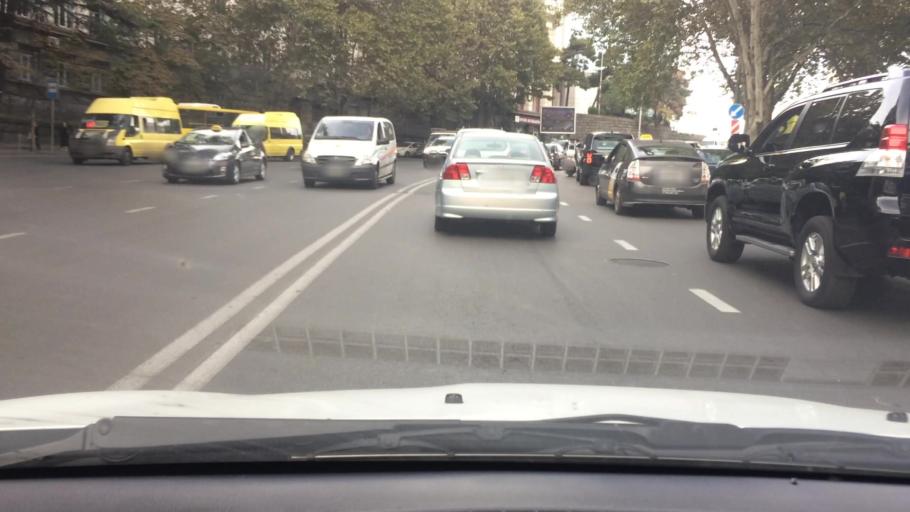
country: GE
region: T'bilisi
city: Tbilisi
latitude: 41.7158
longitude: 44.7789
